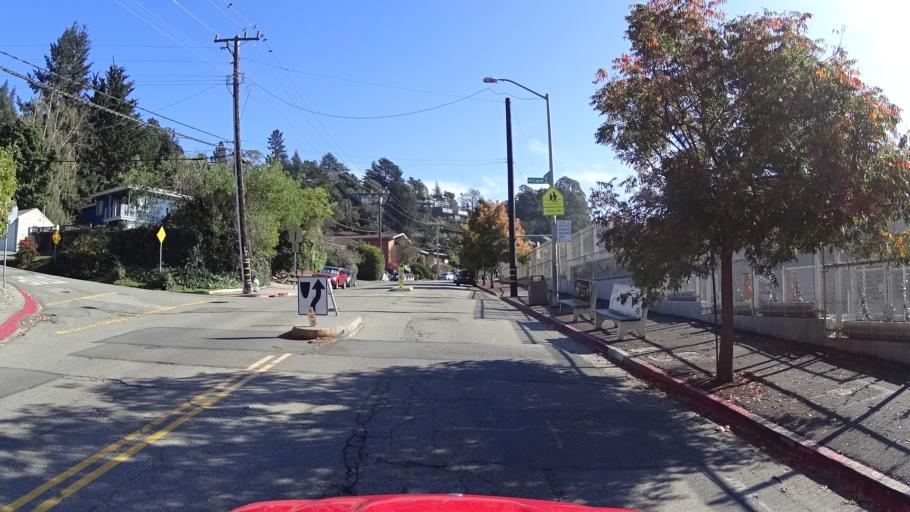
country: US
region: California
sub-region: Alameda County
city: Piedmont
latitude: 37.8307
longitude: -122.2121
